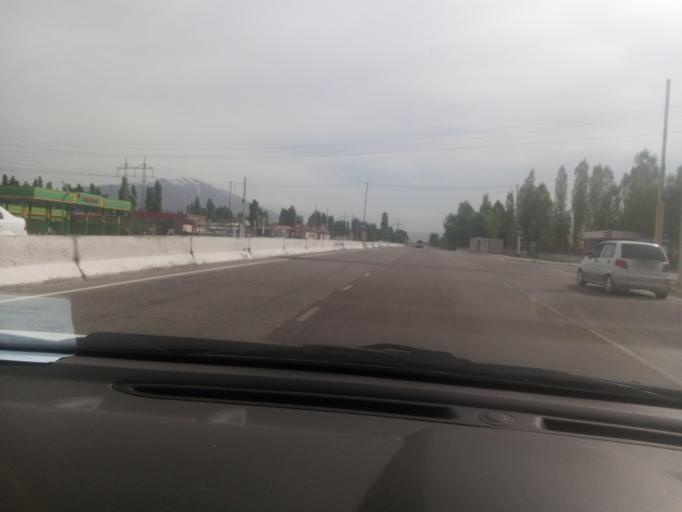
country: UZ
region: Toshkent
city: Angren
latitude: 40.9842
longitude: 70.0266
